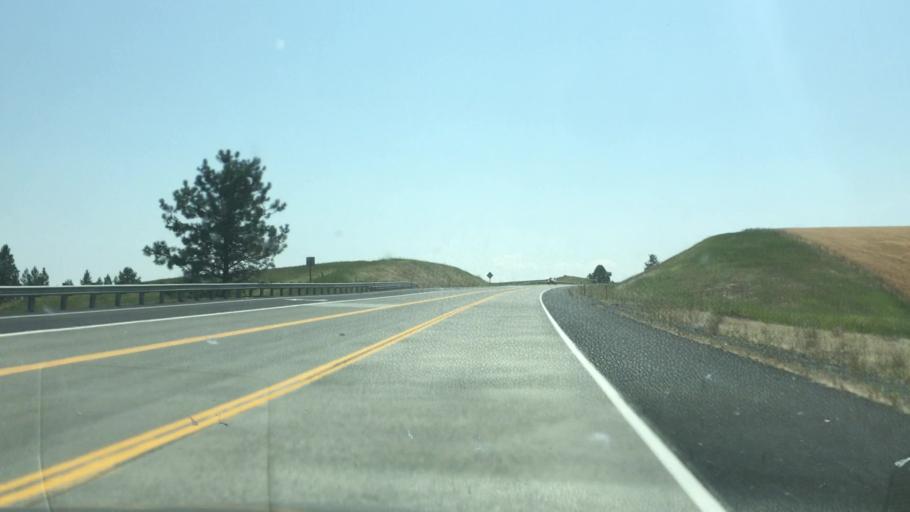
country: US
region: Idaho
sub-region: Lewis County
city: Nezperce
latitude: 46.0990
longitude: -116.3512
